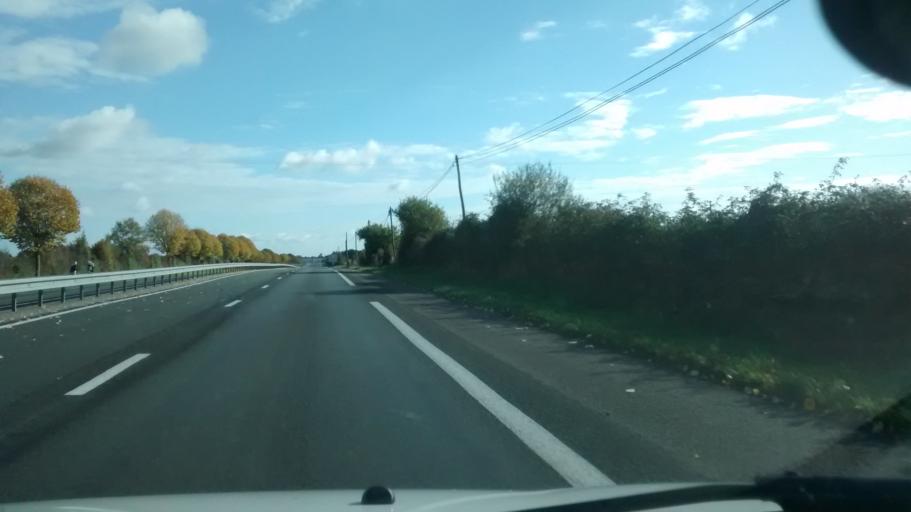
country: FR
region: Pays de la Loire
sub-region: Departement de Maine-et-Loire
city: Pouance
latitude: 47.7330
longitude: -1.1281
